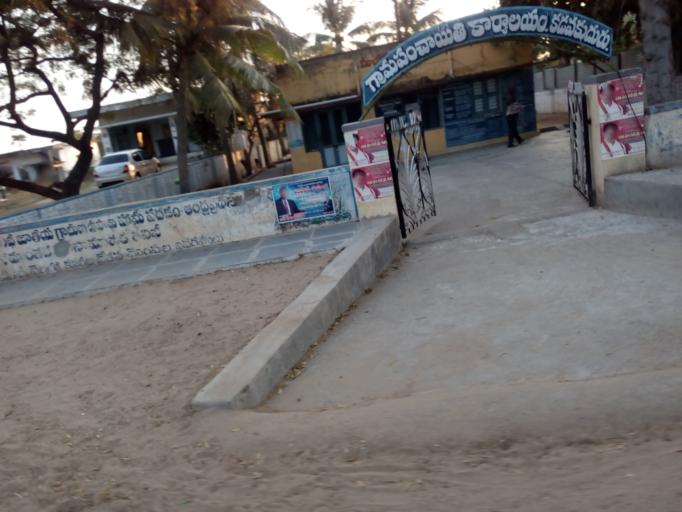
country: IN
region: Andhra Pradesh
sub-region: Prakasam
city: Vetapalem
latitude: 15.7245
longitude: 80.2564
